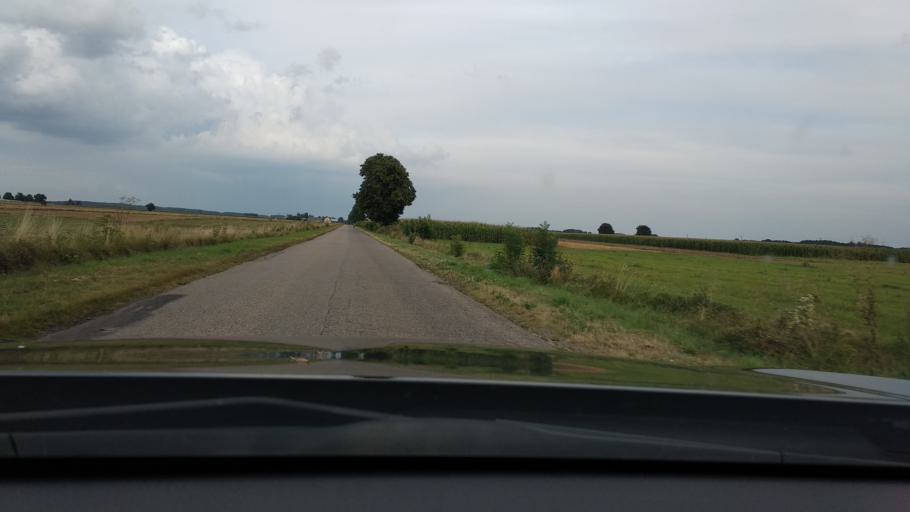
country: PL
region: Masovian Voivodeship
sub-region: Powiat pultuski
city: Obryte
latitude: 52.7185
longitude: 21.2727
